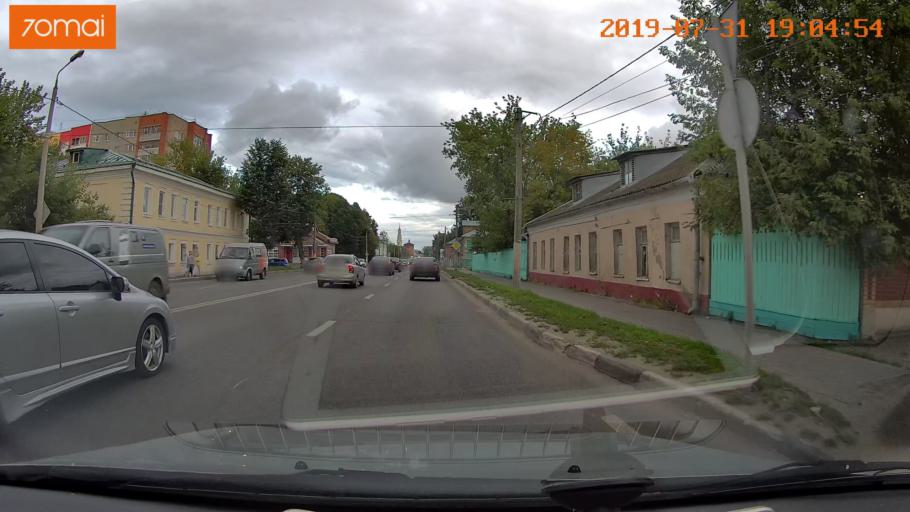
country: RU
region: Moskovskaya
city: Raduzhnyy
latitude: 55.1077
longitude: 38.7431
